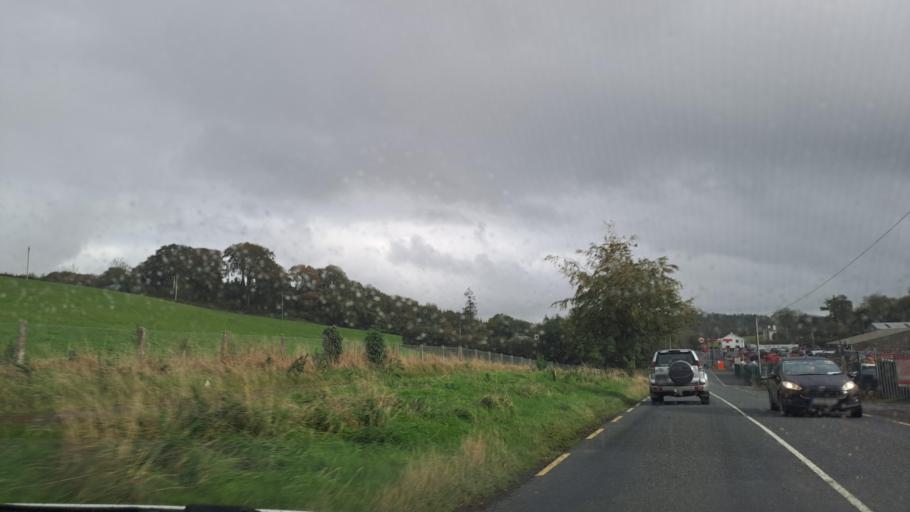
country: IE
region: Ulster
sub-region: An Cabhan
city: Bailieborough
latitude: 53.9212
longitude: -6.9977
